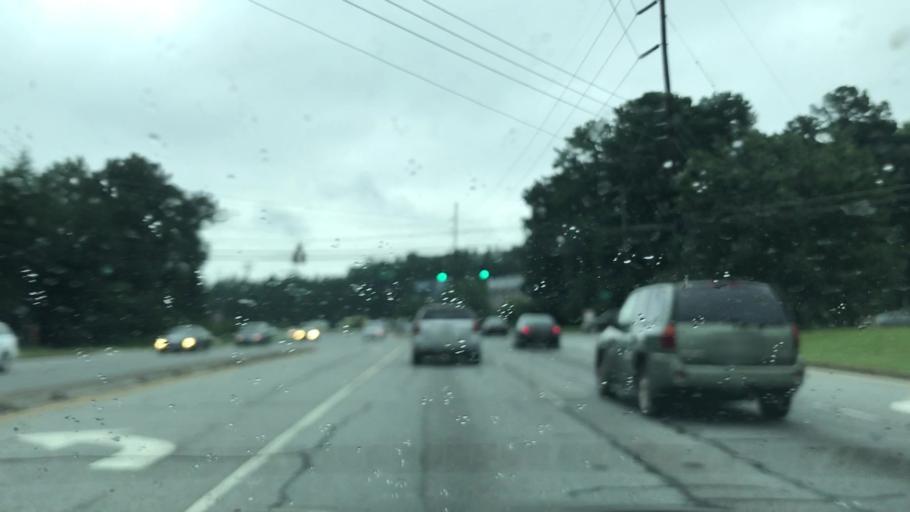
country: US
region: Georgia
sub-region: Gwinnett County
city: Lilburn
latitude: 33.9246
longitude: -84.1381
